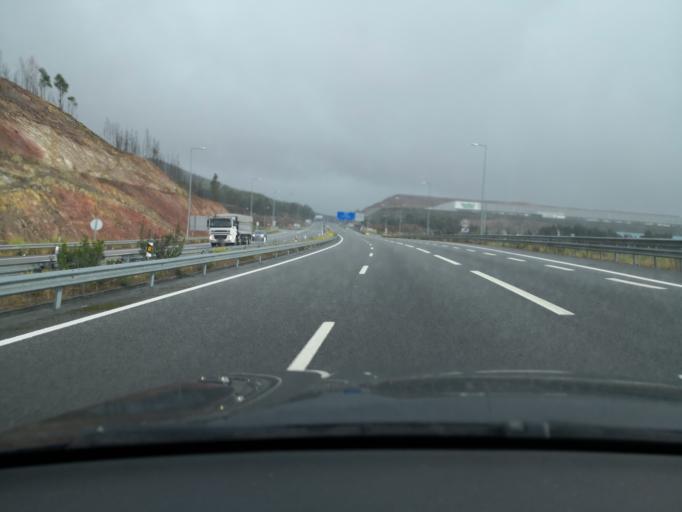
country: PT
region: Porto
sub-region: Valongo
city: Alfena
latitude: 41.2415
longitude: -8.4985
